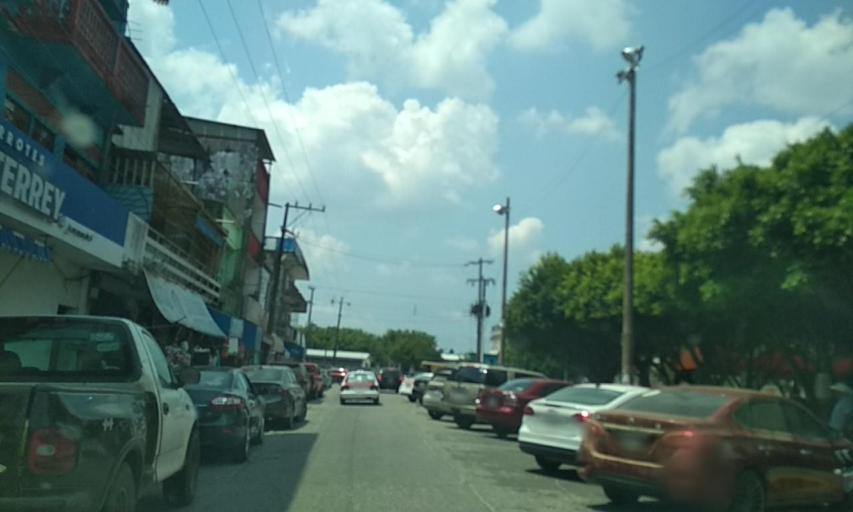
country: MX
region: Veracruz
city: Las Choapas
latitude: 17.9085
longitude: -94.0899
